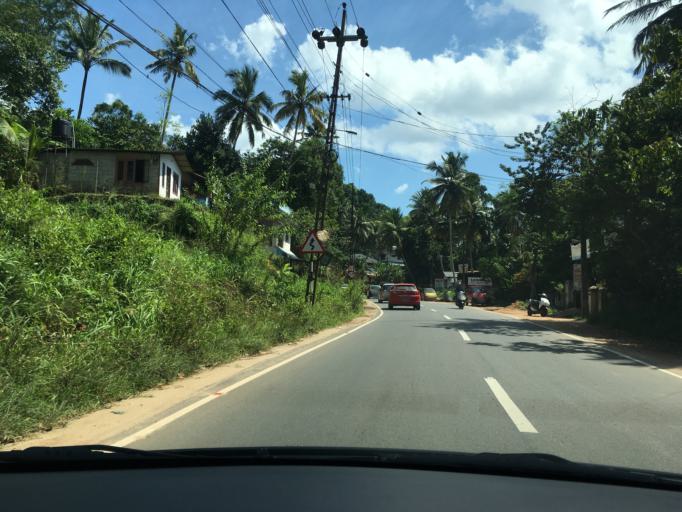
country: IN
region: Kerala
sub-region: Thiruvananthapuram
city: Nedumangad
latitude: 8.5968
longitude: 76.9959
